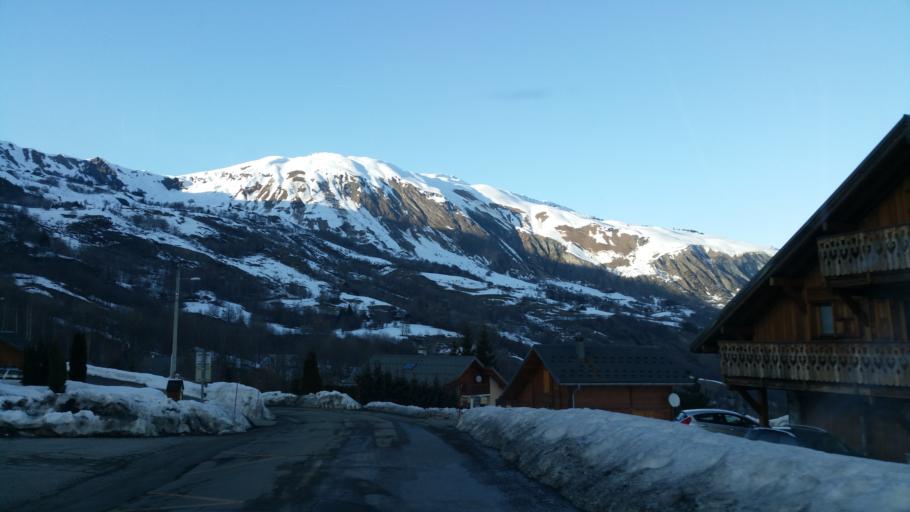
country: FR
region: Rhone-Alpes
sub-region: Departement de la Savoie
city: Saint-Jean-de-Maurienne
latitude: 45.2676
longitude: 6.2981
